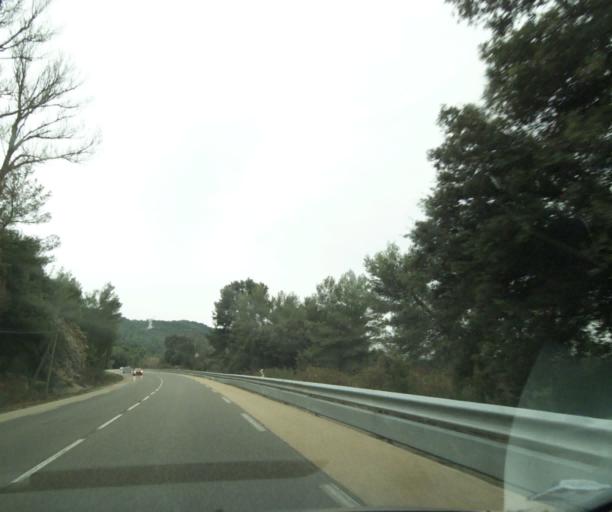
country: FR
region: Provence-Alpes-Cote d'Azur
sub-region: Departement des Bouches-du-Rhone
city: Jouques
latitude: 43.6714
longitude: 5.6489
